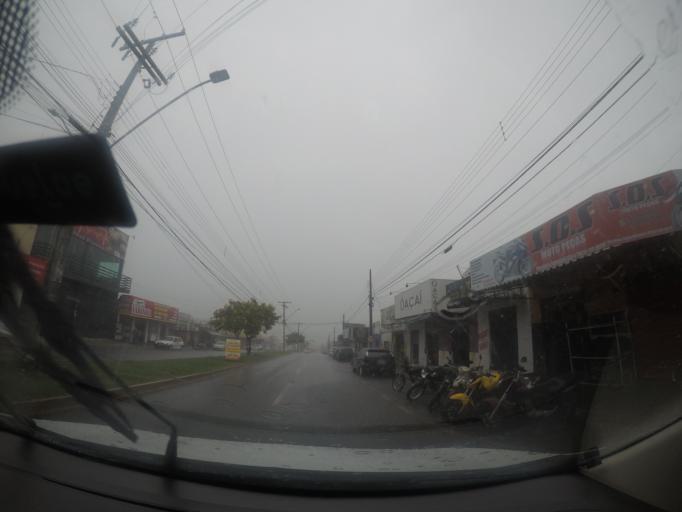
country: BR
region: Goias
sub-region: Goiania
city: Goiania
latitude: -16.6156
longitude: -49.3477
